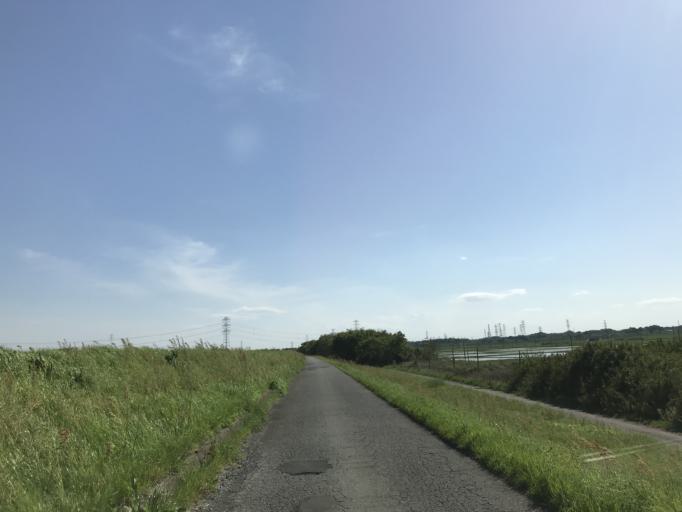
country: JP
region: Ibaraki
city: Moriya
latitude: 35.9586
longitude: 139.9451
